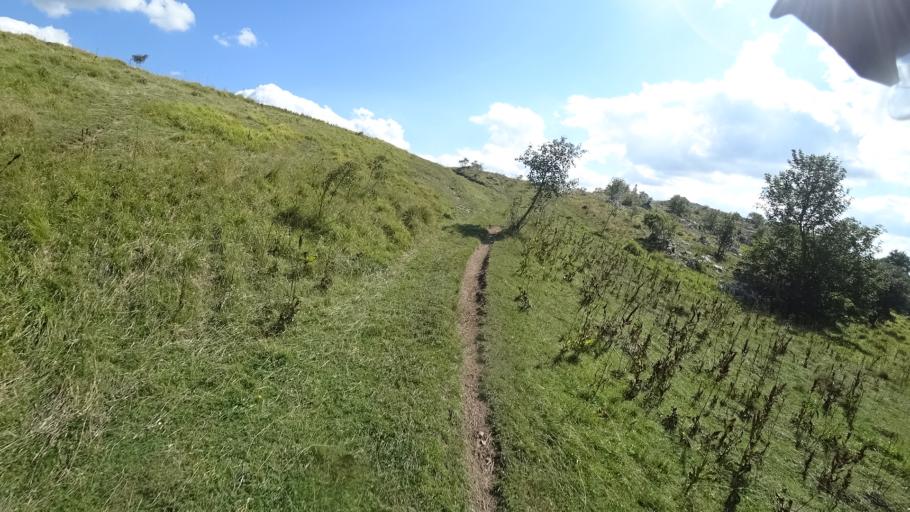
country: HR
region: Zadarska
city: Gracac
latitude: 44.4035
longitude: 16.0072
